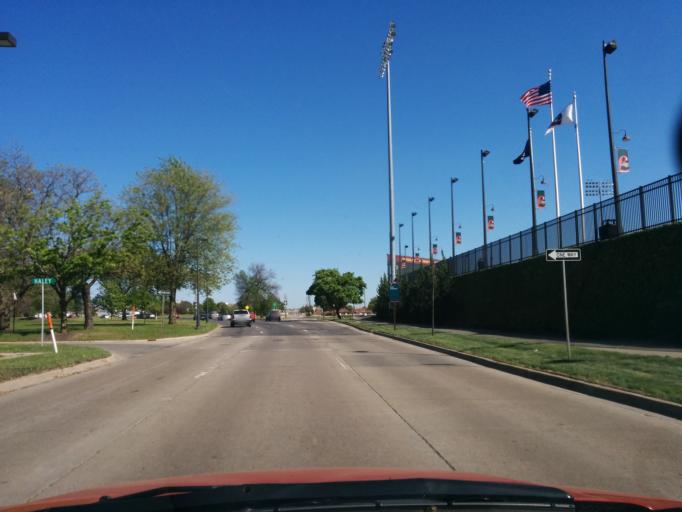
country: US
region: Michigan
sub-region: Midland County
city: Midland
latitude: 43.6100
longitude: -84.2362
